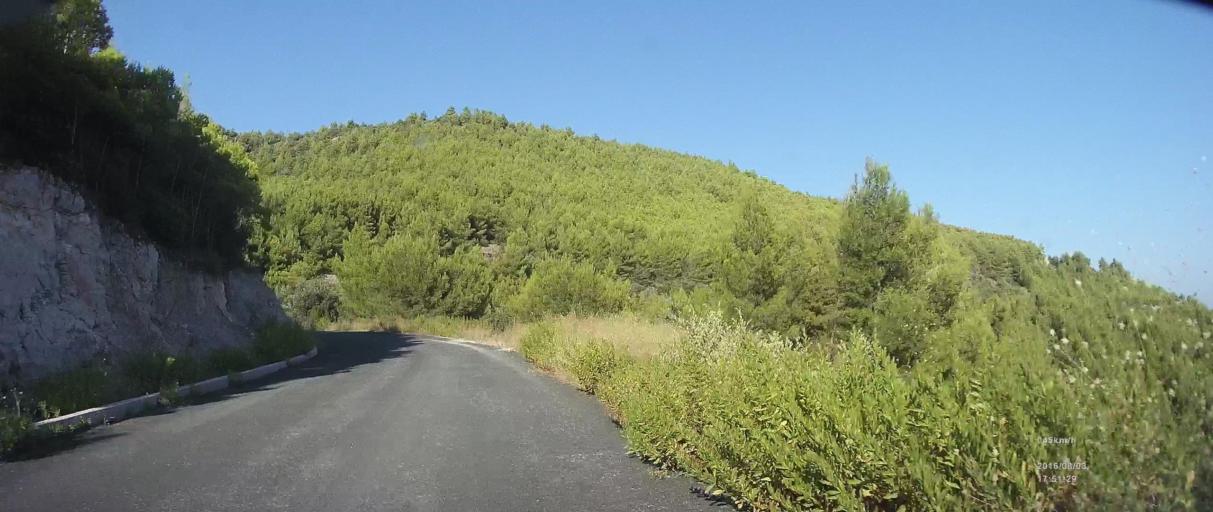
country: HR
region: Dubrovacko-Neretvanska
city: Blato
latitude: 42.7391
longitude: 17.5280
